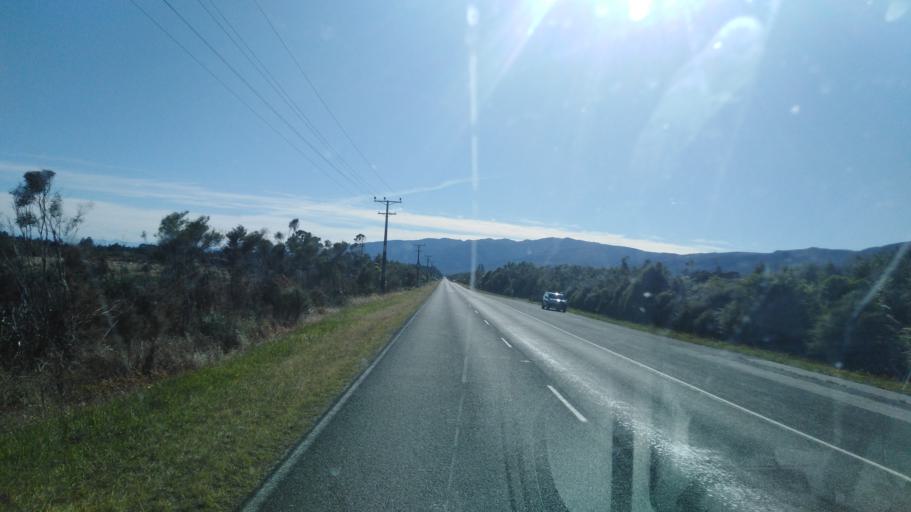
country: NZ
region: West Coast
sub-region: Buller District
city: Westport
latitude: -41.7493
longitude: 171.6755
